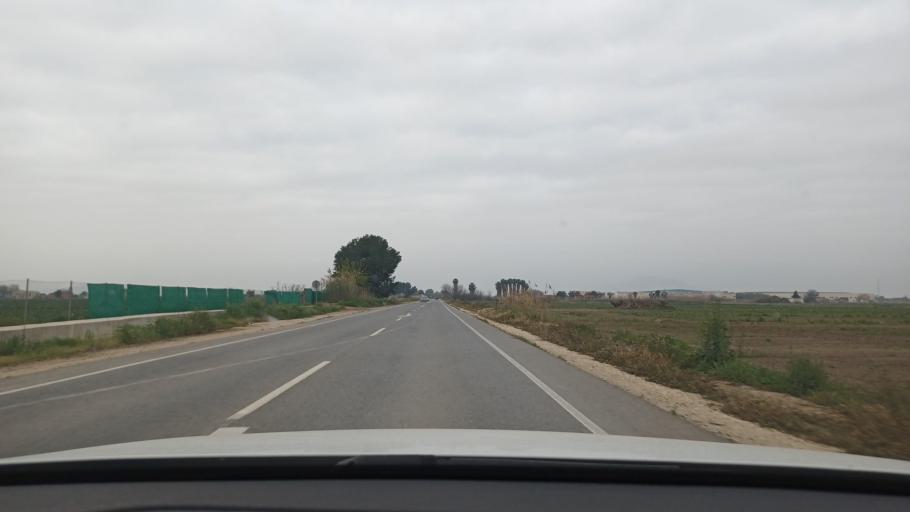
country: ES
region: Valencia
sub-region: Provincia de Alicante
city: Daya Vieja
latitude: 38.1447
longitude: -0.7299
